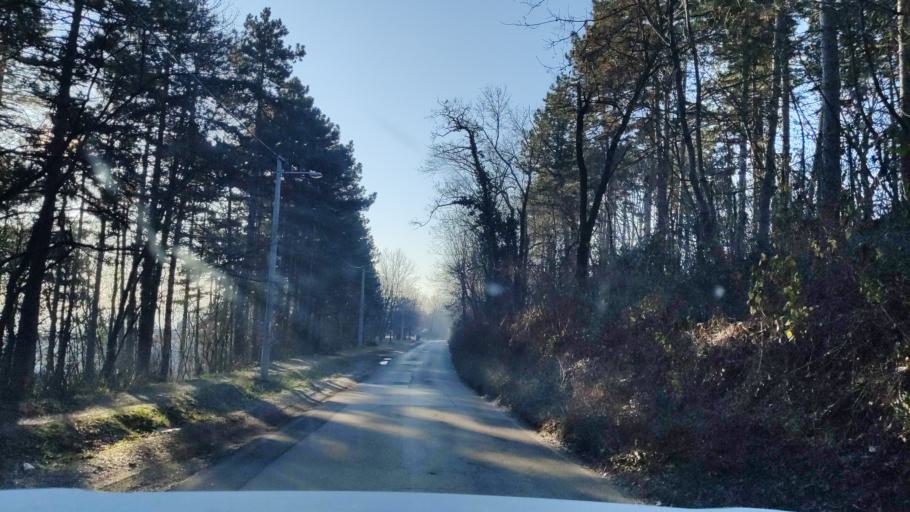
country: RS
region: Central Serbia
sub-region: Belgrade
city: Palilula
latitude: 44.8010
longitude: 20.5149
